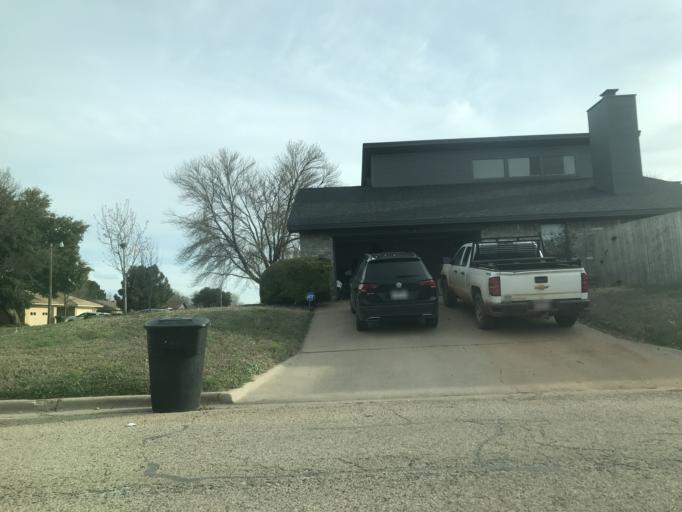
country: US
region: Texas
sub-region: Taylor County
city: Abilene
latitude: 32.3982
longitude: -99.7706
